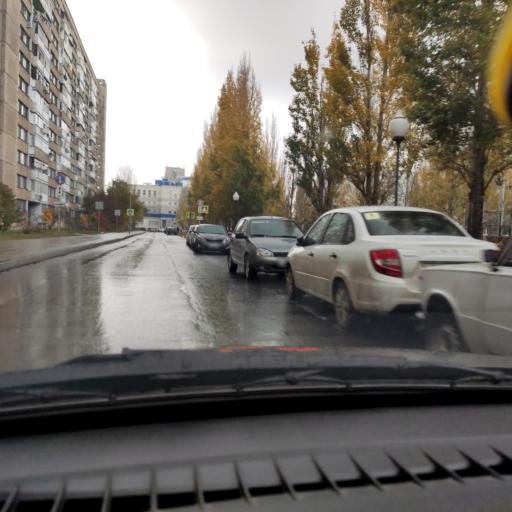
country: RU
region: Samara
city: Tol'yatti
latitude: 53.5310
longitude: 49.3187
